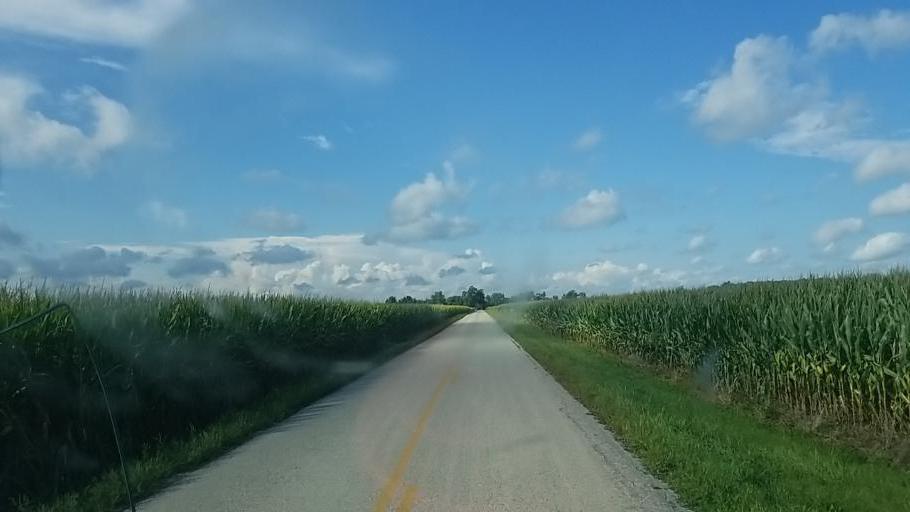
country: US
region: Ohio
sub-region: Hardin County
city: Forest
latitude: 40.7241
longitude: -83.5145
